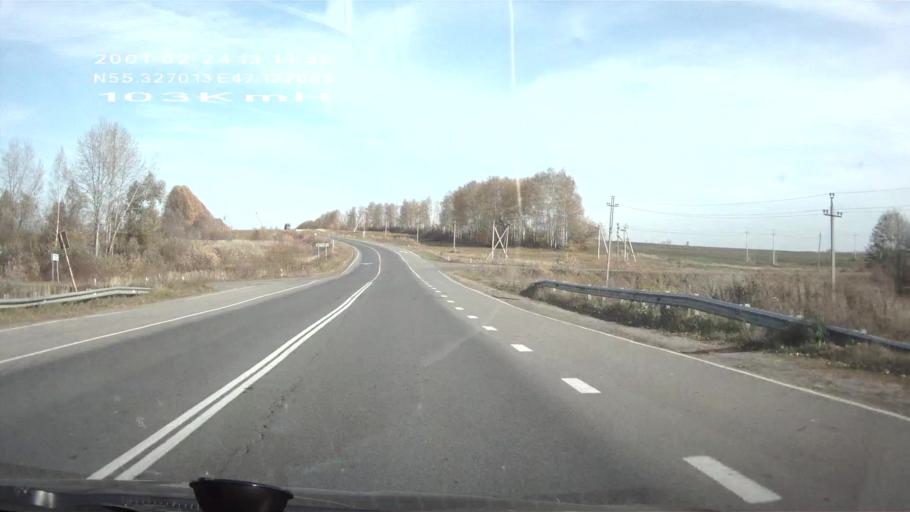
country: RU
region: Chuvashia
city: Ibresi
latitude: 55.3271
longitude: 47.1228
